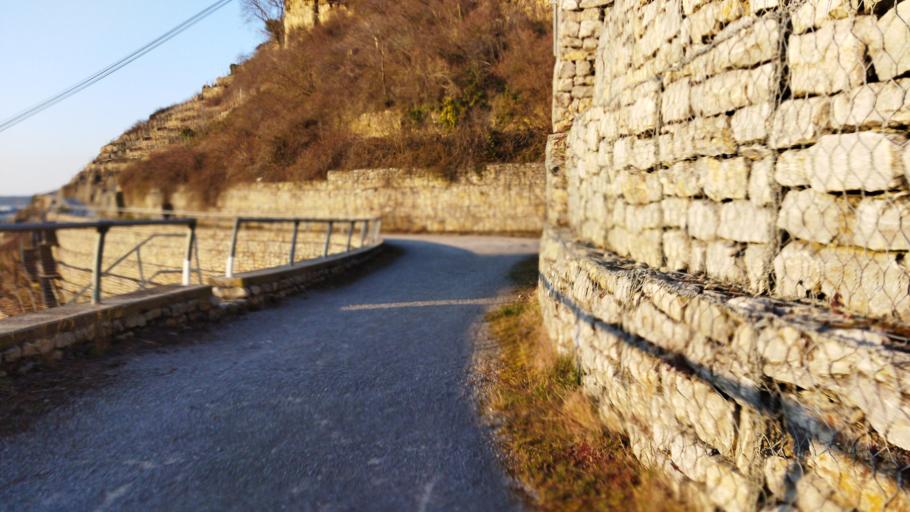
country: DE
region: Baden-Wuerttemberg
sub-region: Regierungsbezirk Stuttgart
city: Walheim
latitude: 49.0165
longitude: 9.1618
